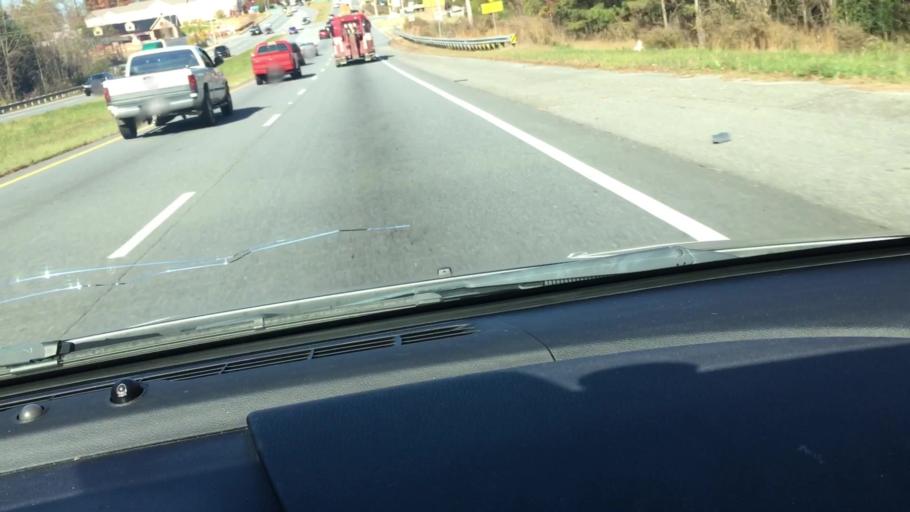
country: US
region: Georgia
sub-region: Fulton County
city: Milton
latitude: 34.1219
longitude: -84.2233
